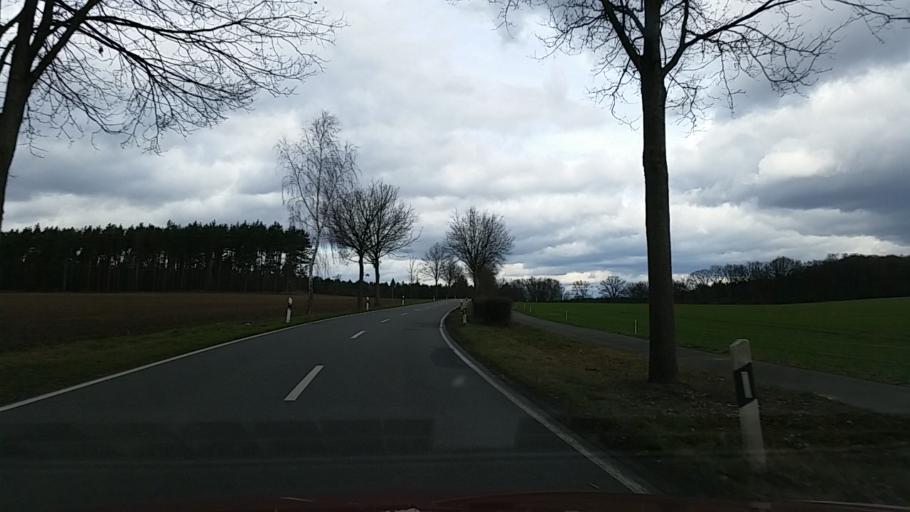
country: DE
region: Lower Saxony
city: Zernien
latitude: 53.0933
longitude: 10.9450
